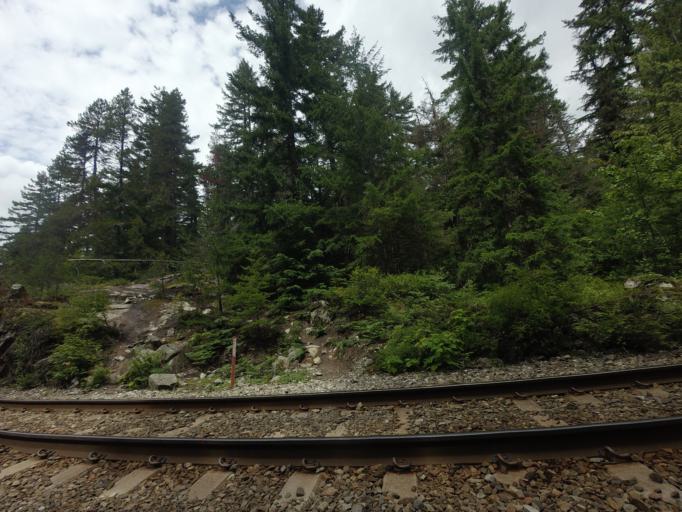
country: CA
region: British Columbia
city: Whistler
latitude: 50.0804
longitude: -123.0572
